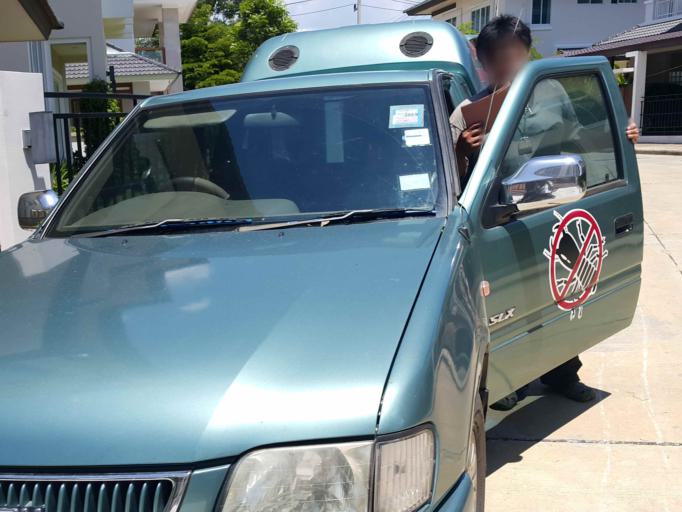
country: TH
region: Chiang Mai
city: Saraphi
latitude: 18.7541
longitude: 99.0406
